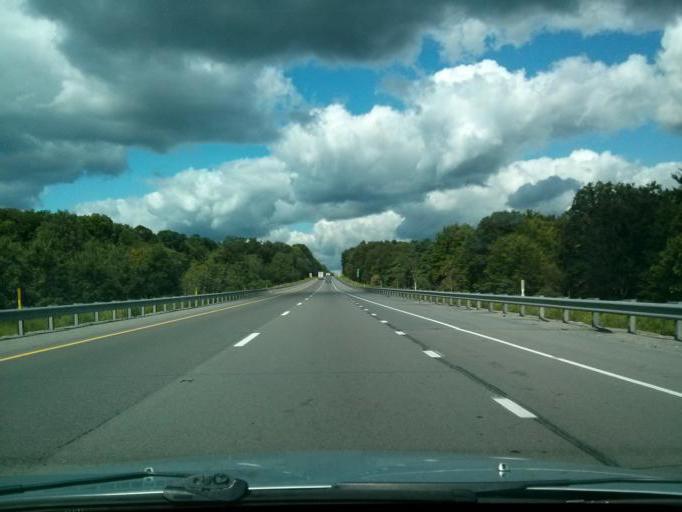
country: US
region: Pennsylvania
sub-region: Clearfield County
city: Treasure Lake
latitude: 41.1319
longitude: -78.7154
